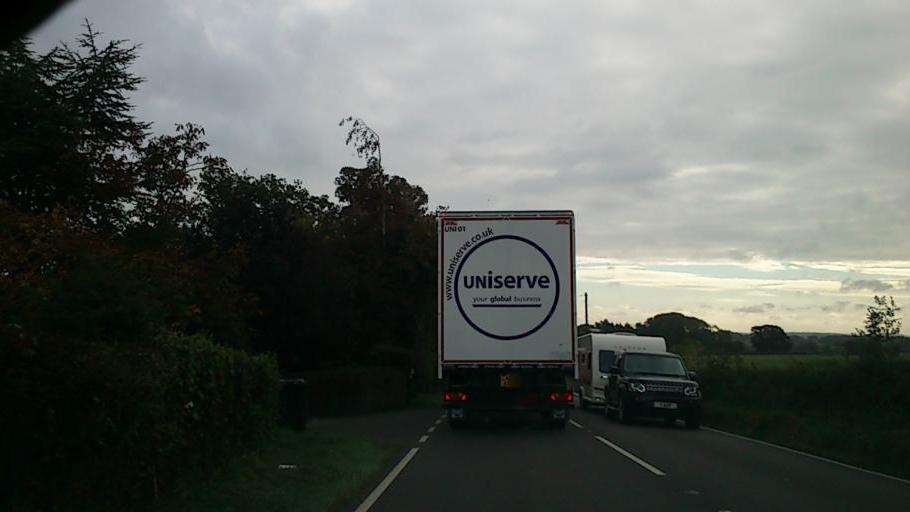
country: GB
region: England
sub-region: Shropshire
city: Westbury
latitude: 52.7070
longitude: -2.9300
